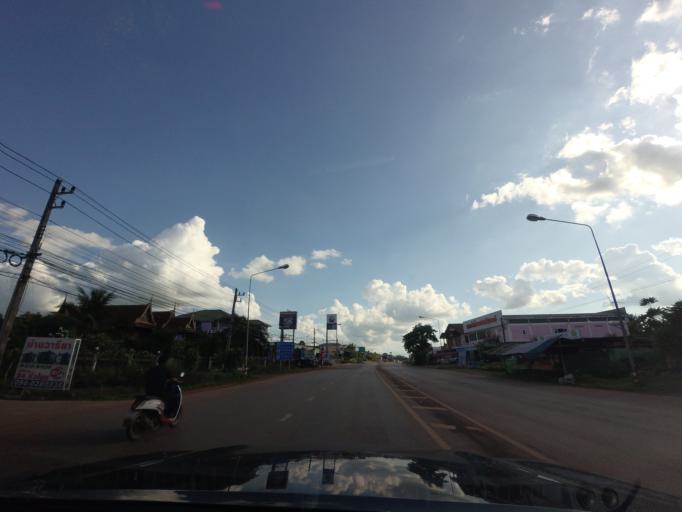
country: TH
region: Changwat Udon Thani
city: Ban Dung
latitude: 17.6792
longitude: 103.2545
